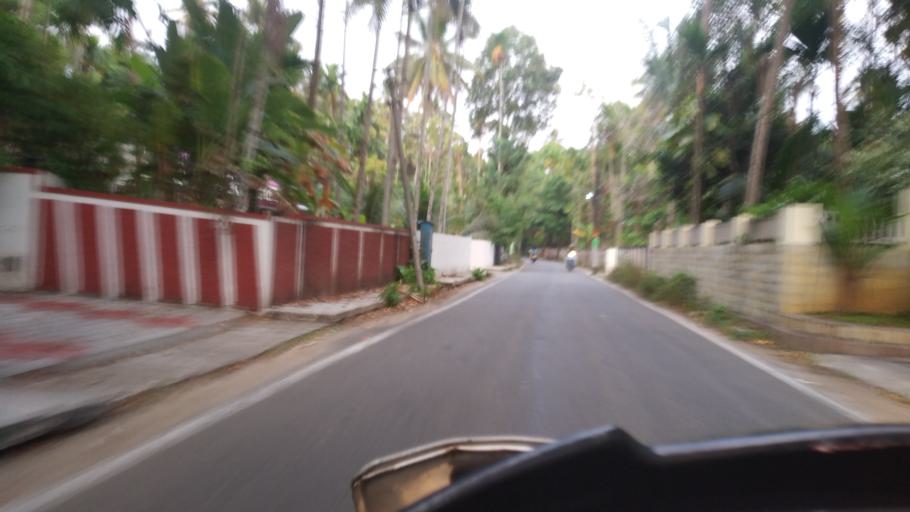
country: IN
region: Kerala
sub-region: Thrissur District
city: Kodungallur
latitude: 10.1665
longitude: 76.1995
